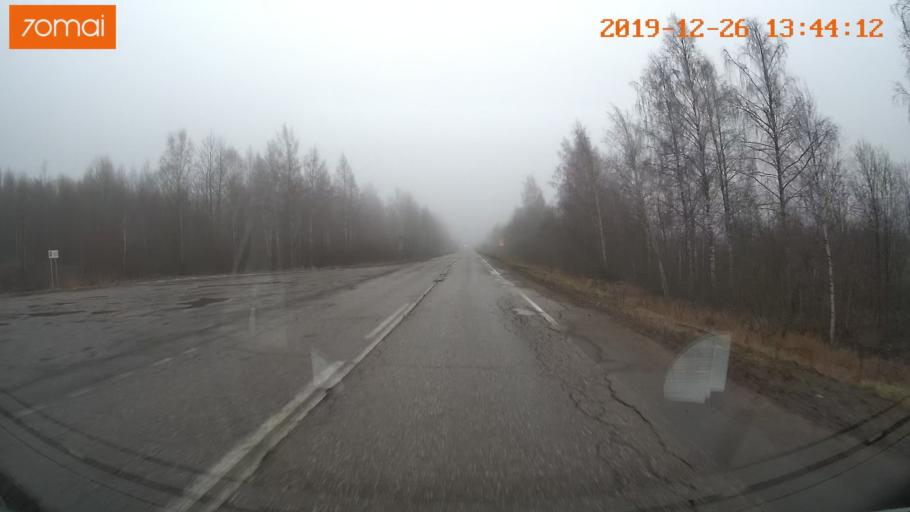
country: RU
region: Vologda
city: Sheksna
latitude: 58.7037
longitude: 38.5034
